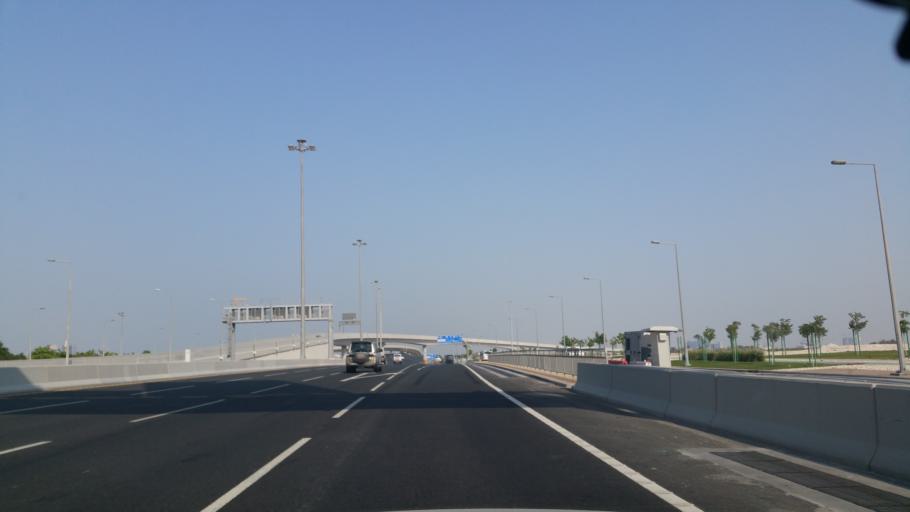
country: QA
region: Baladiyat ar Rayyan
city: Ar Rayyan
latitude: 25.2949
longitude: 51.4679
